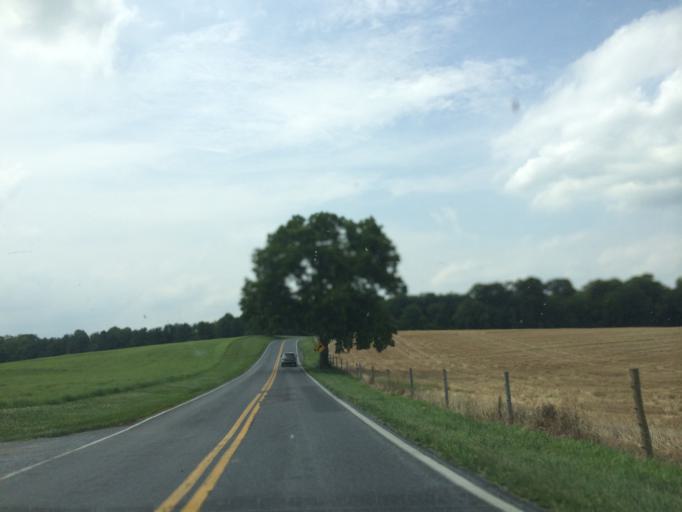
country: US
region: Maryland
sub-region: Montgomery County
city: Olney
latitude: 39.2634
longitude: -77.0693
